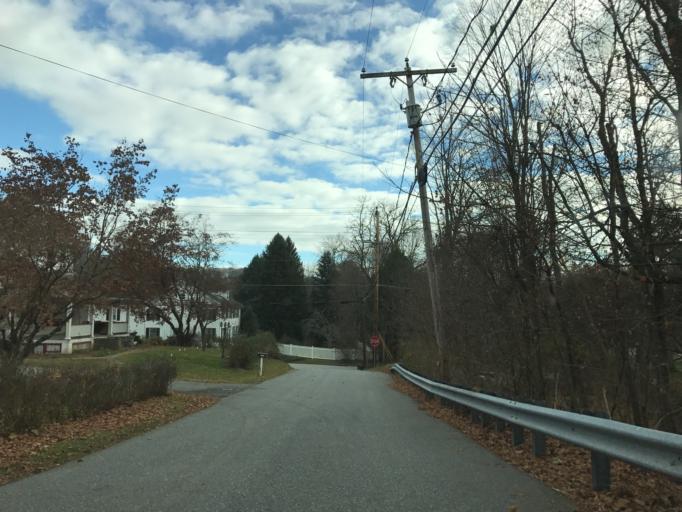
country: US
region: Maryland
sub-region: Baltimore County
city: Hunt Valley
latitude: 39.6200
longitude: -76.6268
